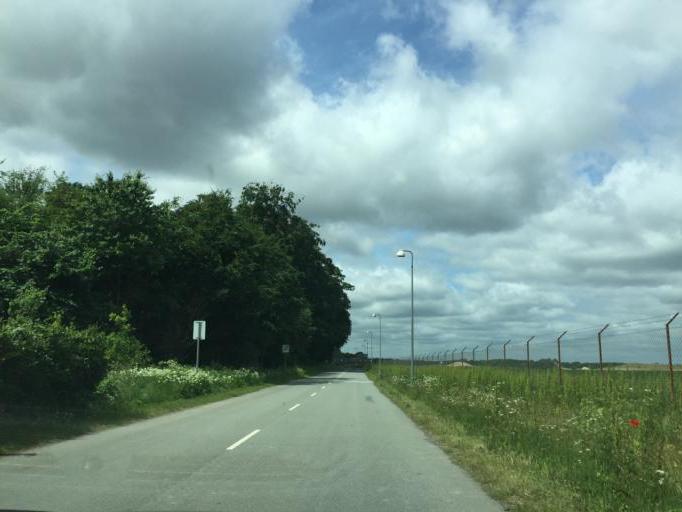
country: DK
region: South Denmark
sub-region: Odense Kommune
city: Hojby
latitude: 55.3563
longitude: 10.4353
